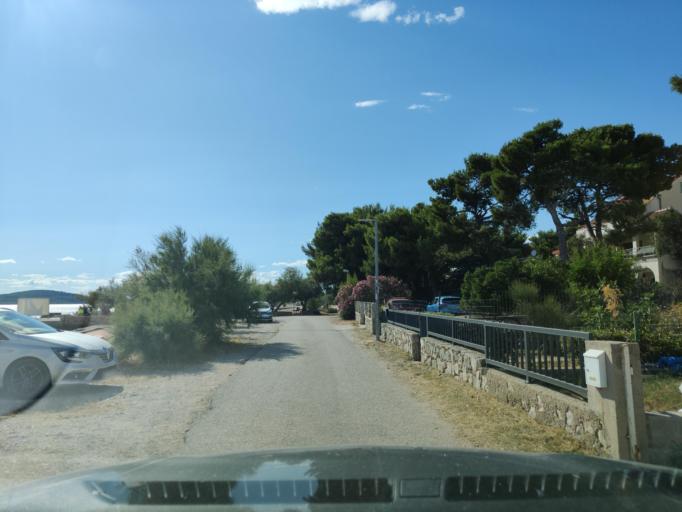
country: HR
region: Sibensko-Kniniska
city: Zaton
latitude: 43.7272
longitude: 15.8386
